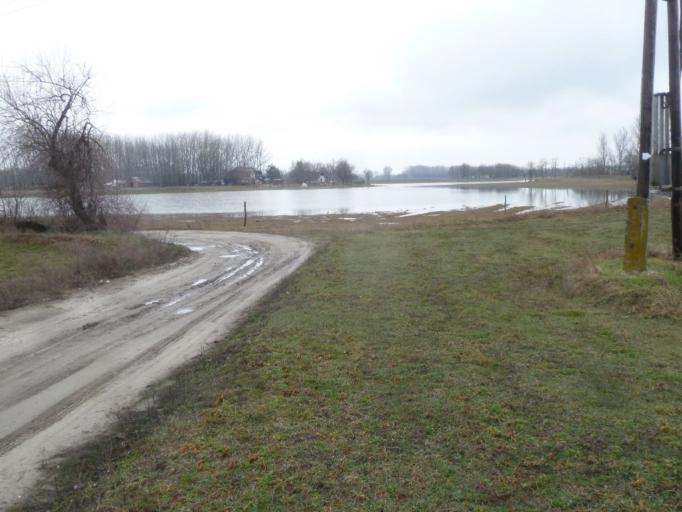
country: HU
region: Bacs-Kiskun
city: Bugac
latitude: 46.7227
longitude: 19.6189
